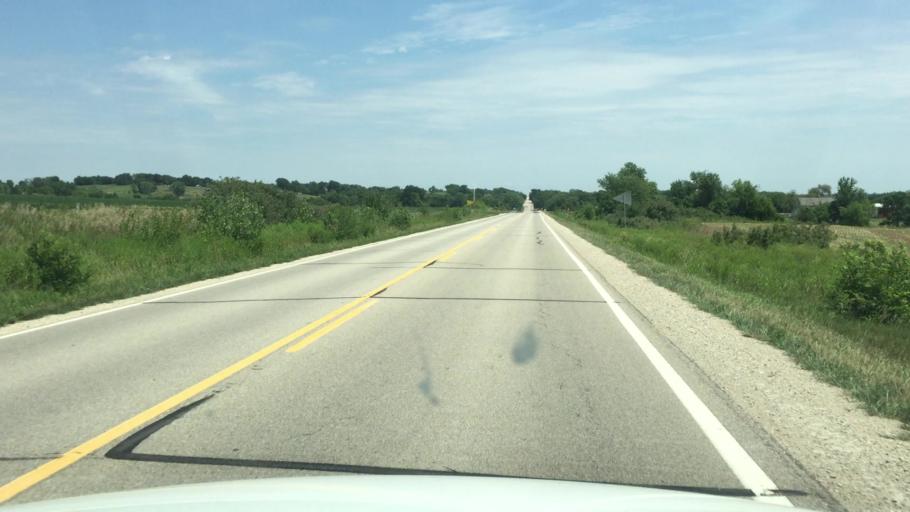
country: US
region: Kansas
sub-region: Osage County
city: Overbrook
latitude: 38.9712
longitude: -95.4700
